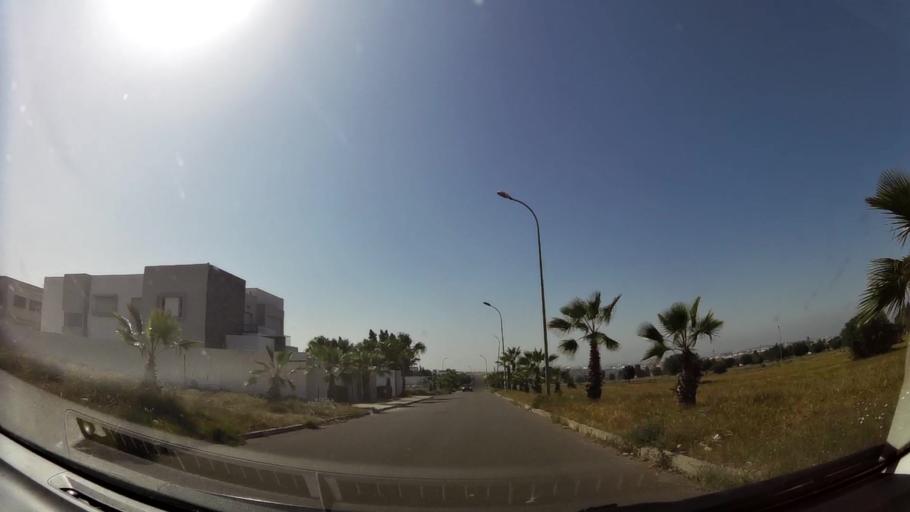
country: MA
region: Souss-Massa-Draa
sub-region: Agadir-Ida-ou-Tnan
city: Agadir
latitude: 30.4394
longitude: -9.5810
